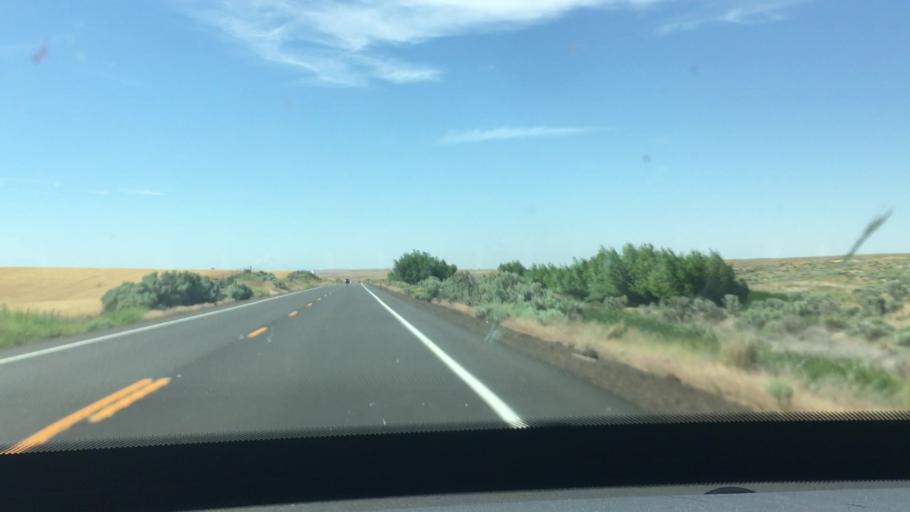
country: US
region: Oregon
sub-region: Sherman County
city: Moro
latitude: 45.3340
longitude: -120.7702
